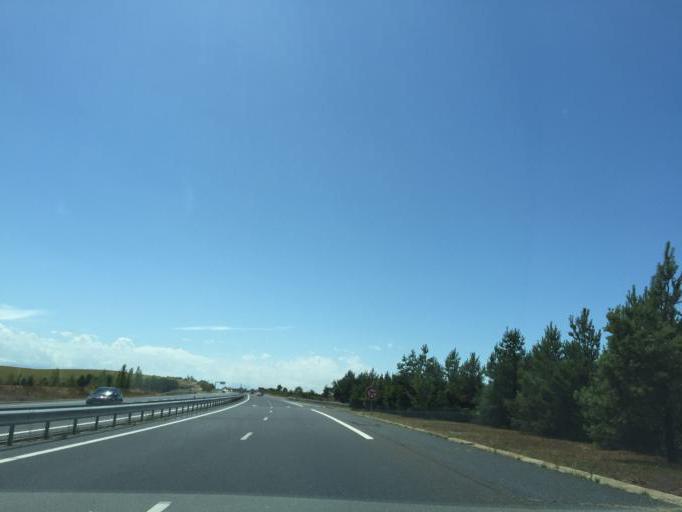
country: FR
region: Midi-Pyrenees
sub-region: Departement de l'Aveyron
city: Severac-le-Chateau
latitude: 44.2574
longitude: 3.0601
